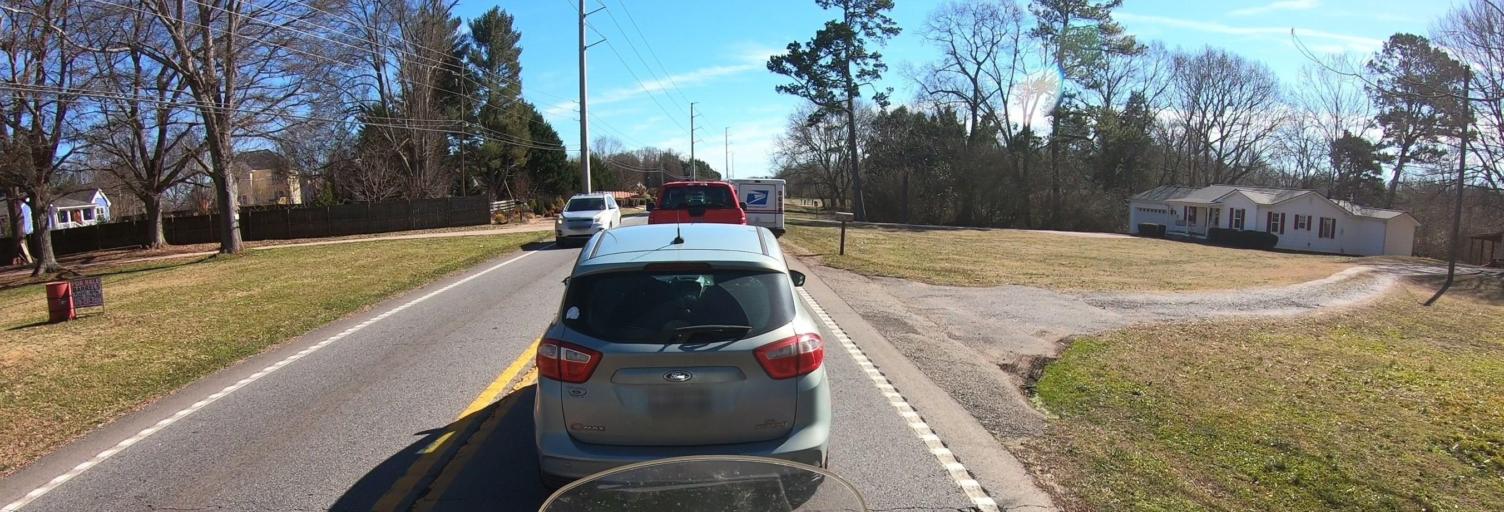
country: US
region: Georgia
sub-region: Forsyth County
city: Cumming
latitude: 34.2810
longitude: -84.1255
